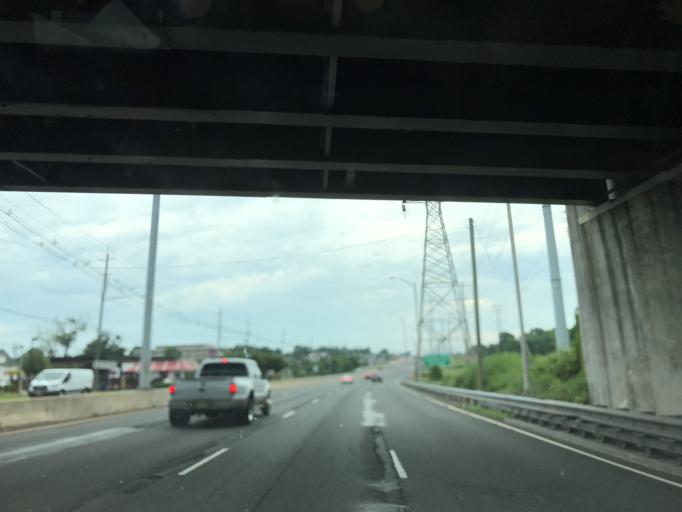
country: US
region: New Jersey
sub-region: Middlesex County
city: Fords
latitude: 40.5426
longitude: -74.3347
